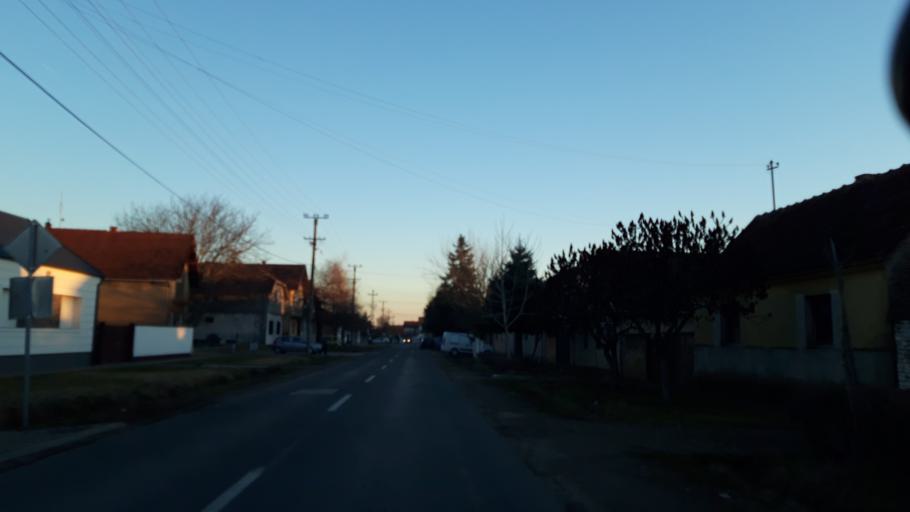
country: RS
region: Autonomna Pokrajina Vojvodina
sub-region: Sremski Okrug
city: Ingija
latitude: 45.0494
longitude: 20.0685
